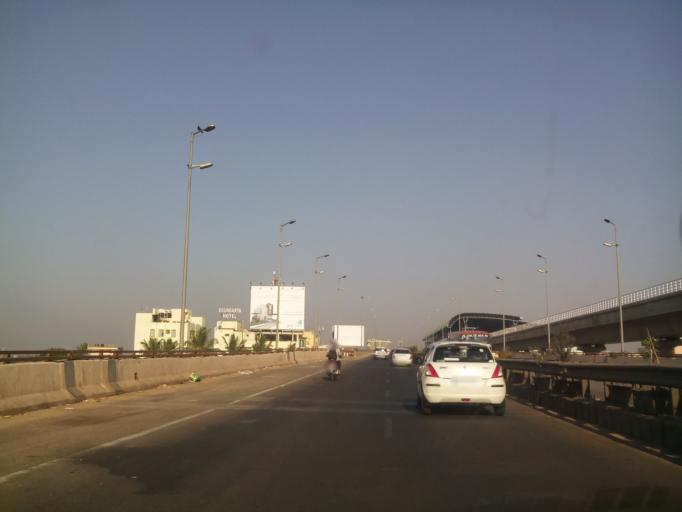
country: IN
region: Karnataka
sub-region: Bangalore Urban
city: Yelahanka
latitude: 13.0423
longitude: 77.5148
